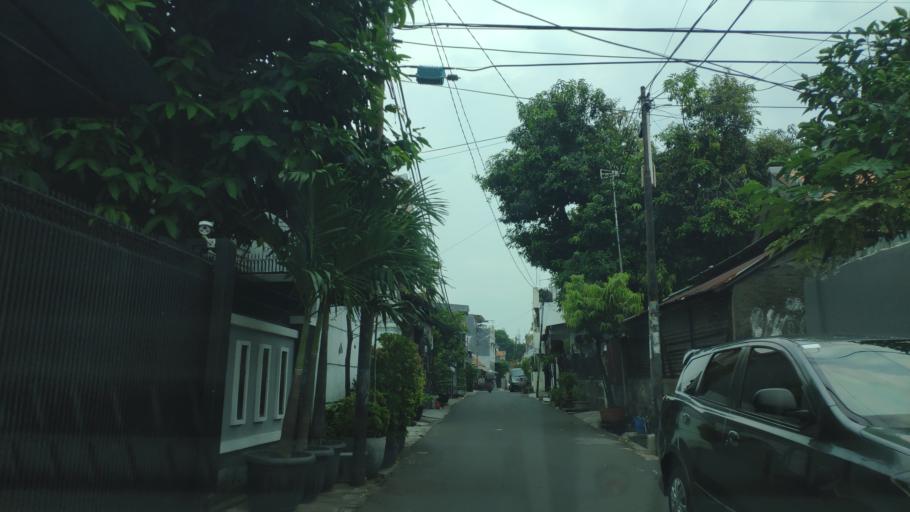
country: ID
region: Jakarta Raya
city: Jakarta
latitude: -6.1922
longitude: 106.8012
